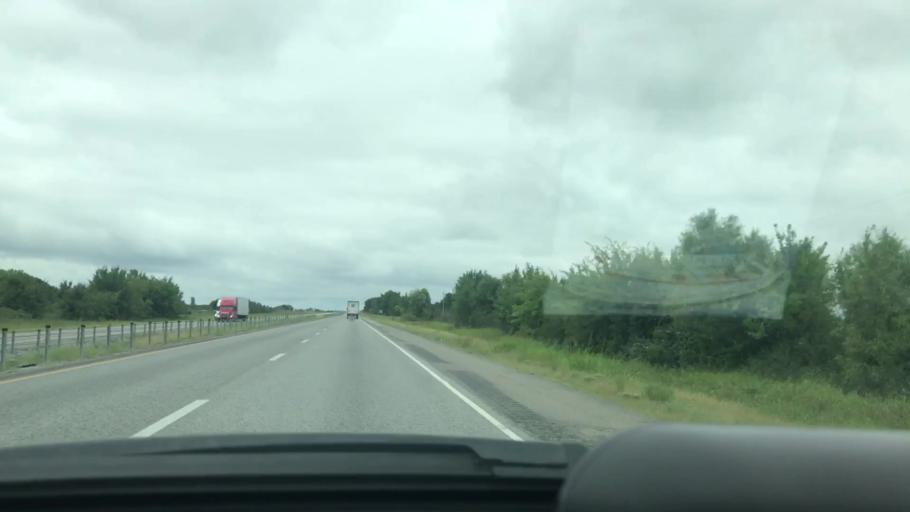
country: US
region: Oklahoma
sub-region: Pittsburg County
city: McAlester
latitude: 34.7443
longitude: -95.8965
